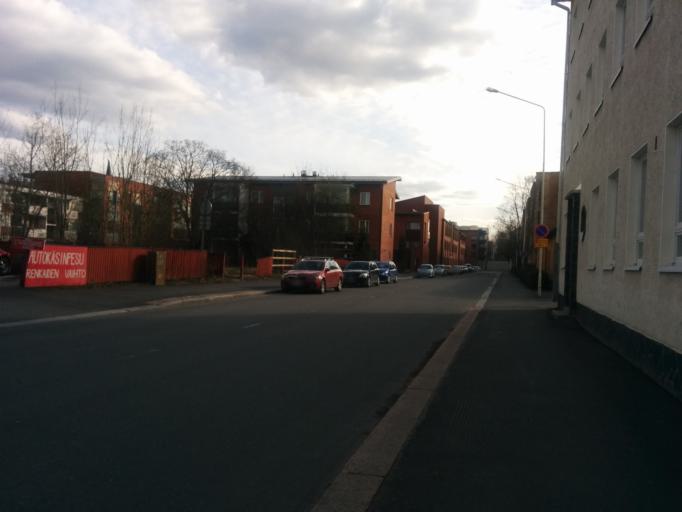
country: FI
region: Haeme
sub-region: Riihimaeki
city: Riihimaeki
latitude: 60.7382
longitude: 24.7711
